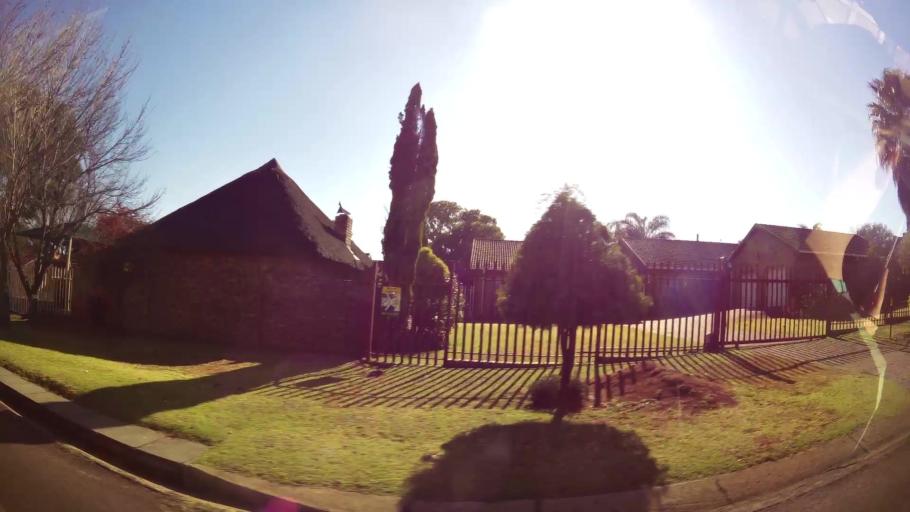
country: ZA
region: Mpumalanga
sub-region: Nkangala District Municipality
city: Witbank
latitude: -25.8899
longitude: 29.2502
